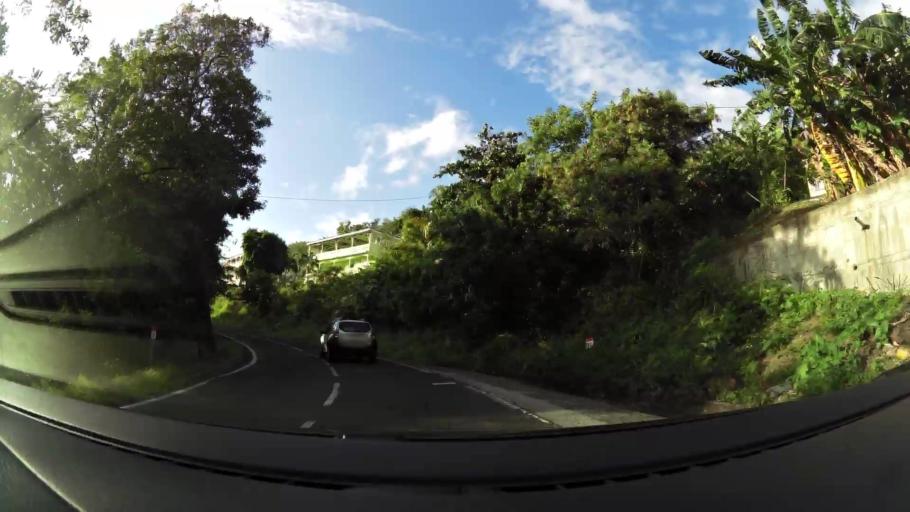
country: GP
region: Guadeloupe
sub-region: Guadeloupe
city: Pointe-Noire
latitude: 16.1821
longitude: -61.7802
